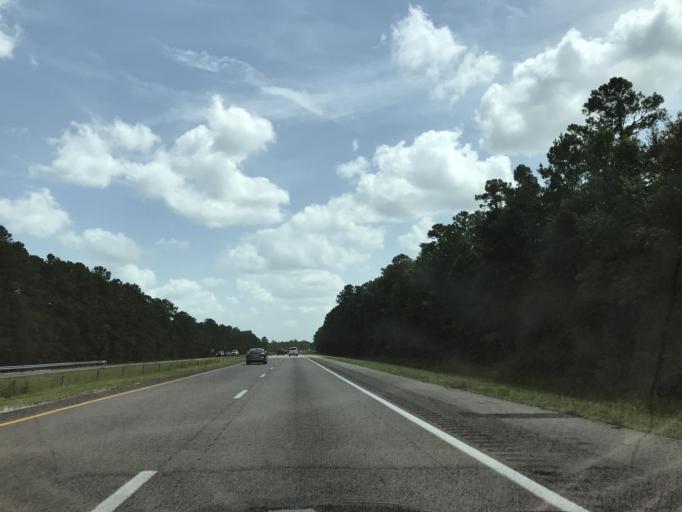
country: US
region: North Carolina
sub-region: Pender County
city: Burgaw
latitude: 34.5935
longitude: -77.9092
